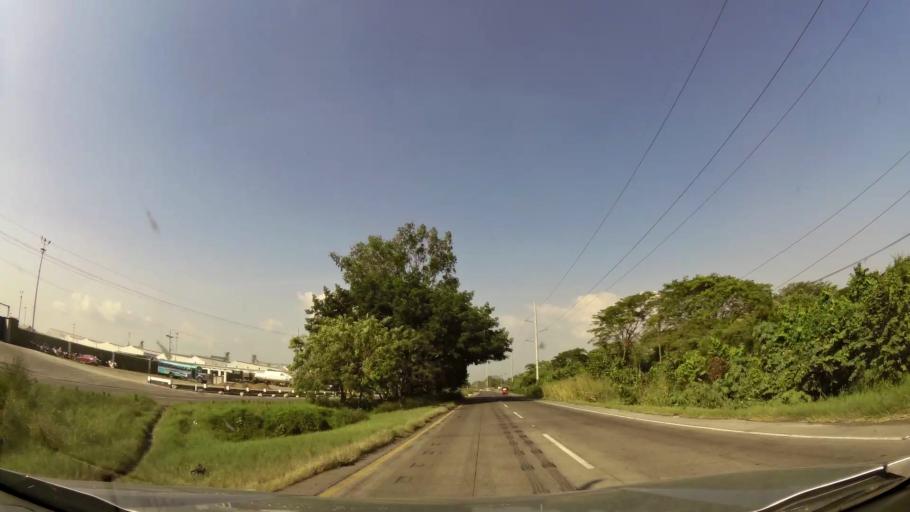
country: GT
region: Escuintla
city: Puerto San Jose
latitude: 13.9595
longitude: -90.7884
